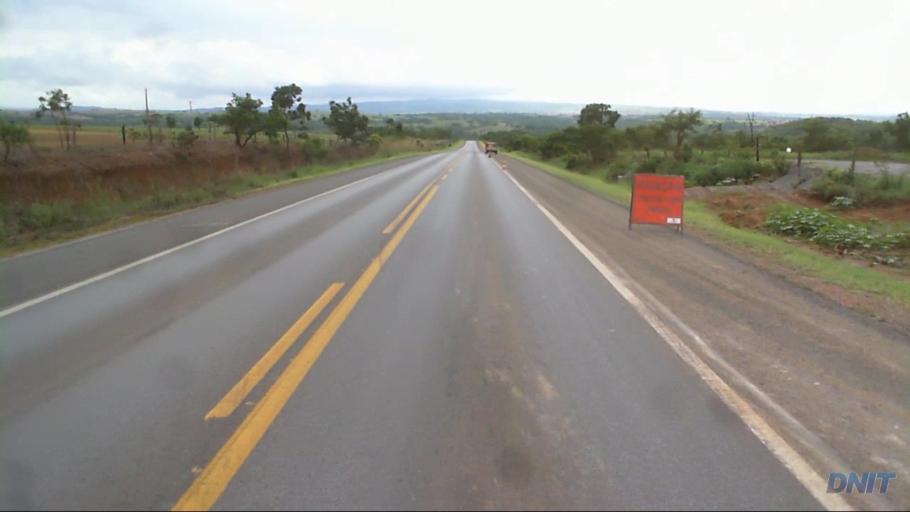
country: BR
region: Goias
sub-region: Padre Bernardo
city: Padre Bernardo
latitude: -15.2159
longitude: -48.6005
